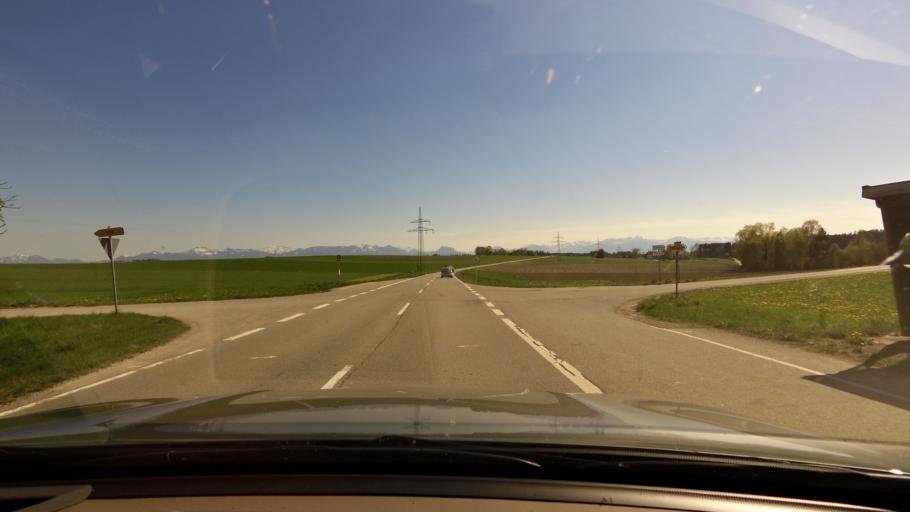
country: DE
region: Bavaria
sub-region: Upper Bavaria
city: Griesstatt
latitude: 47.9788
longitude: 12.1772
